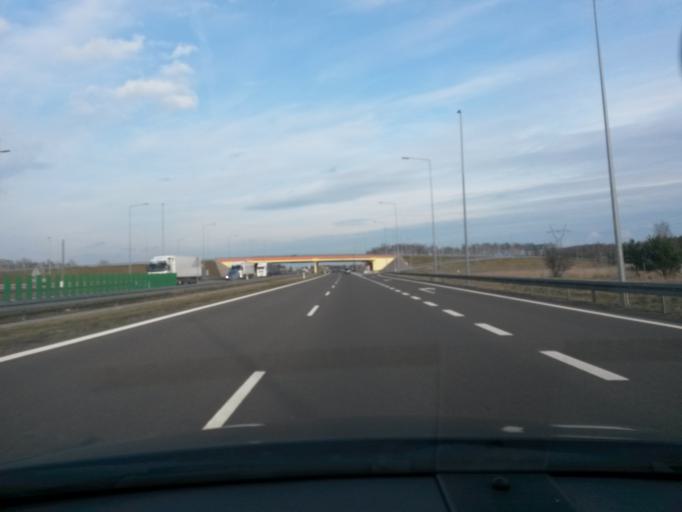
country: PL
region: Lodz Voivodeship
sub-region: Powiat zgierski
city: Ozorkow
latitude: 51.9223
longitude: 19.3496
